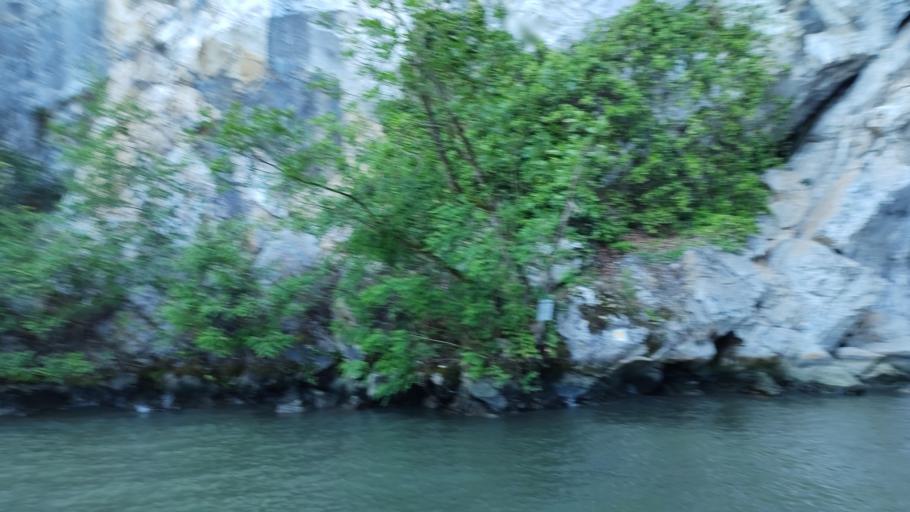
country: RO
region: Mehedinti
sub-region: Comuna Dubova
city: Dubova
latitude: 44.5953
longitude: 22.2612
